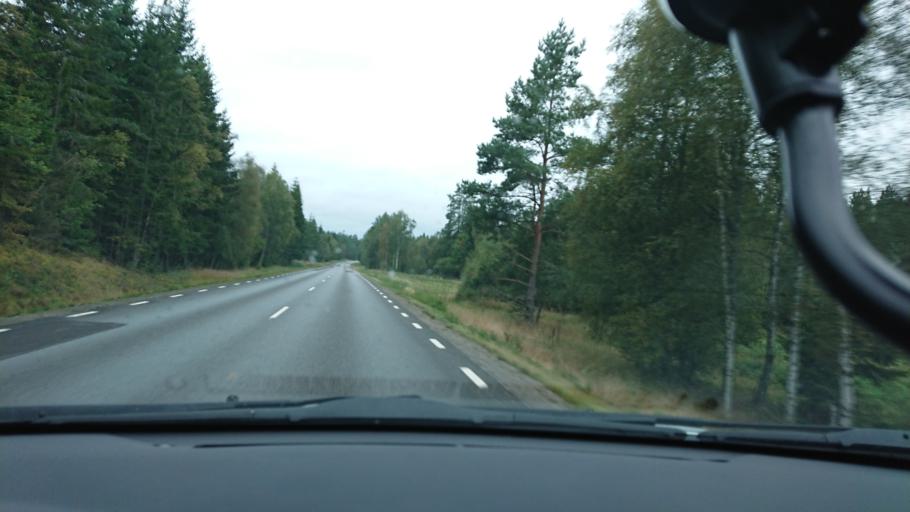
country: SE
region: Kronoberg
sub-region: Vaxjo Kommun
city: Braas
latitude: 57.0249
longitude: 14.9992
